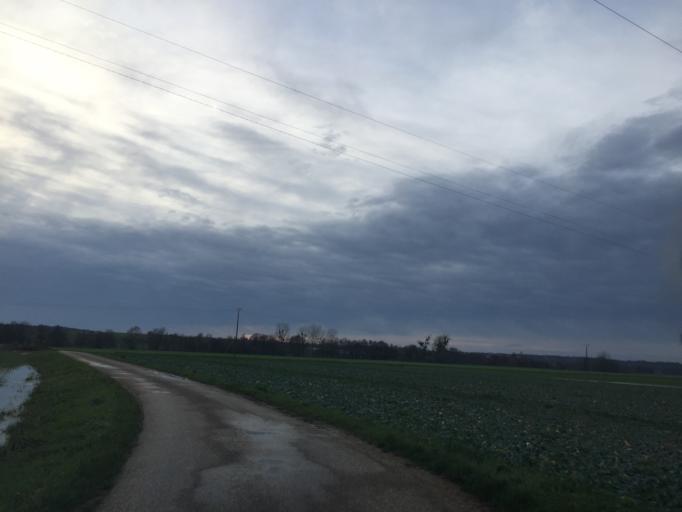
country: FR
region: Franche-Comte
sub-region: Departement du Jura
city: Mont-sous-Vaudrey
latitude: 46.9391
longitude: 5.6781
